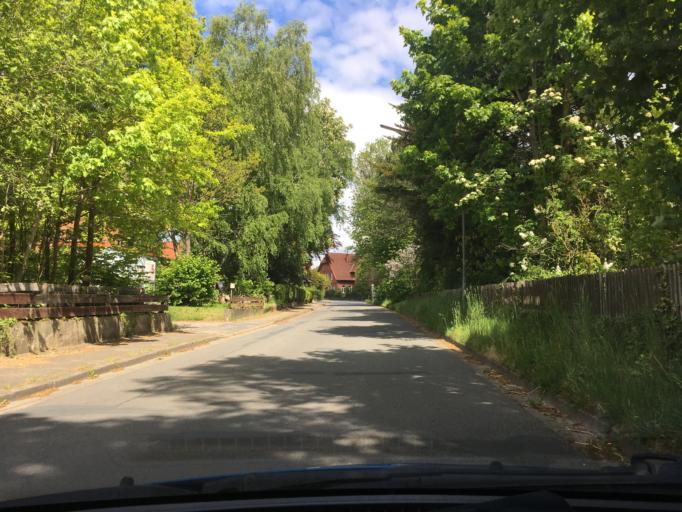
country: DE
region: Lower Saxony
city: Suderburg
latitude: 52.9281
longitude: 10.4431
